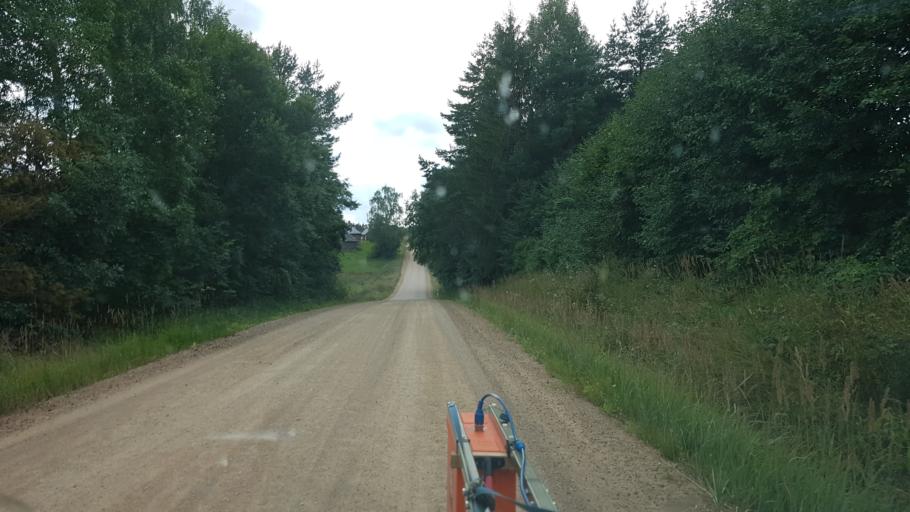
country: RU
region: Pskov
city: Pechory
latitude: 57.7758
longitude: 27.4646
